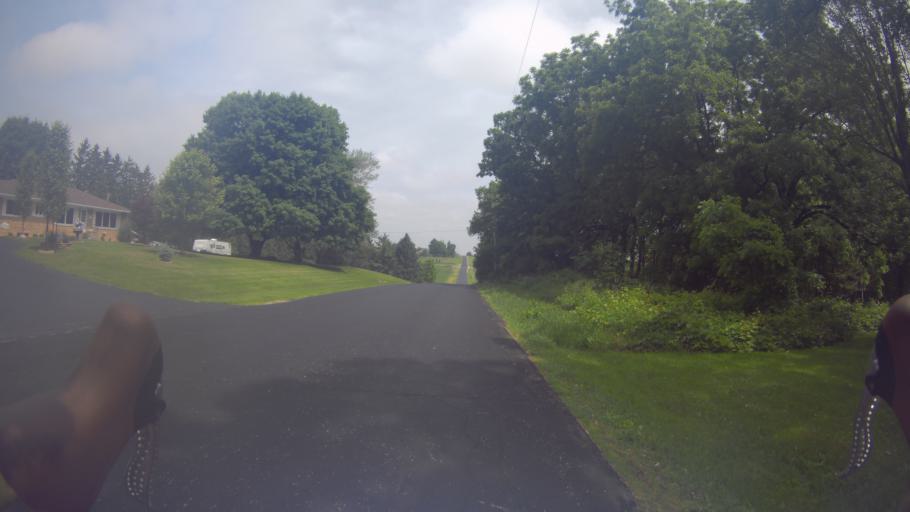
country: US
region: Wisconsin
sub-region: Rock County
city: Edgerton
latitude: 42.9017
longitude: -89.0427
